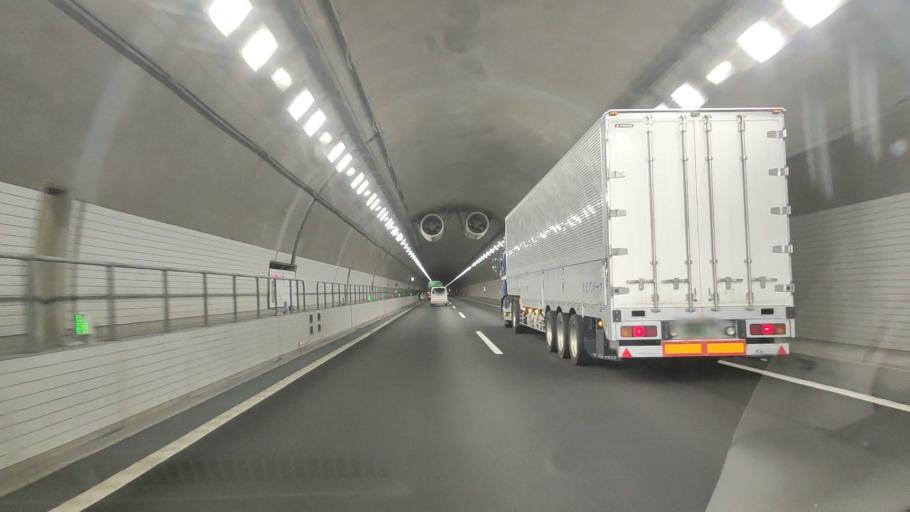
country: JP
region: Tokyo
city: Hachioji
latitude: 35.5748
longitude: 139.2999
